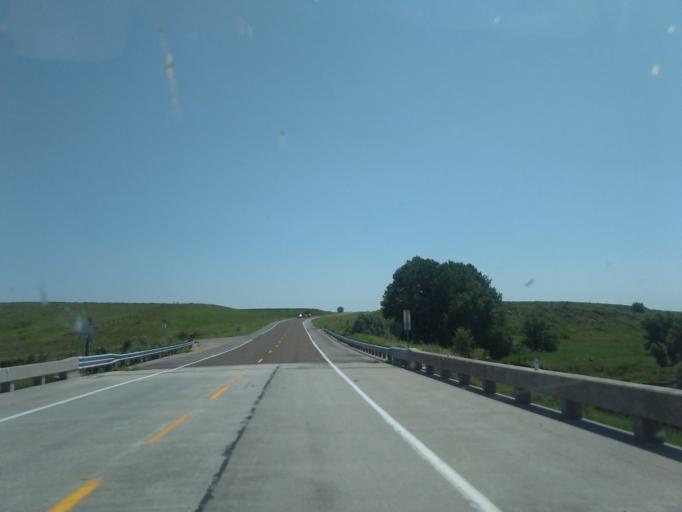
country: US
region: Nebraska
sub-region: Hitchcock County
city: Trenton
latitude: 40.1758
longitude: -101.1362
